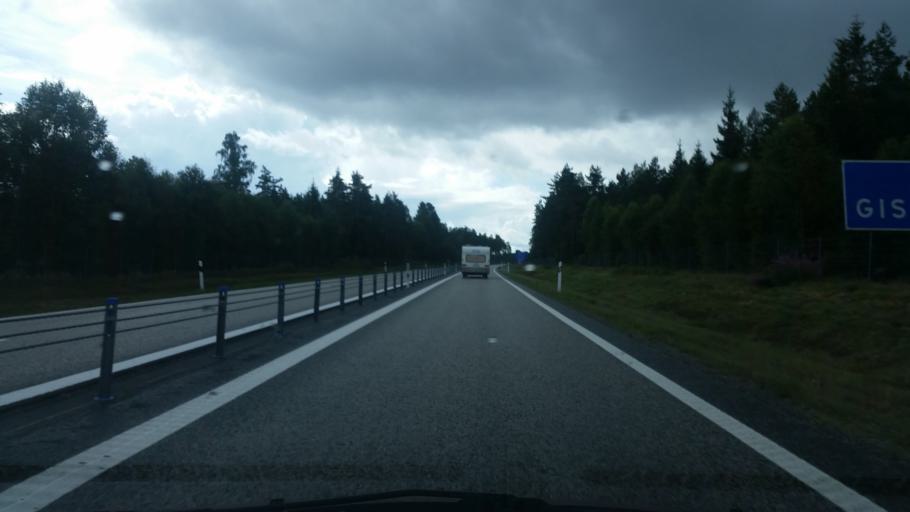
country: SE
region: Joenkoeping
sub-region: Gislaveds Kommun
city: Gislaved
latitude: 57.3324
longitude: 13.5478
